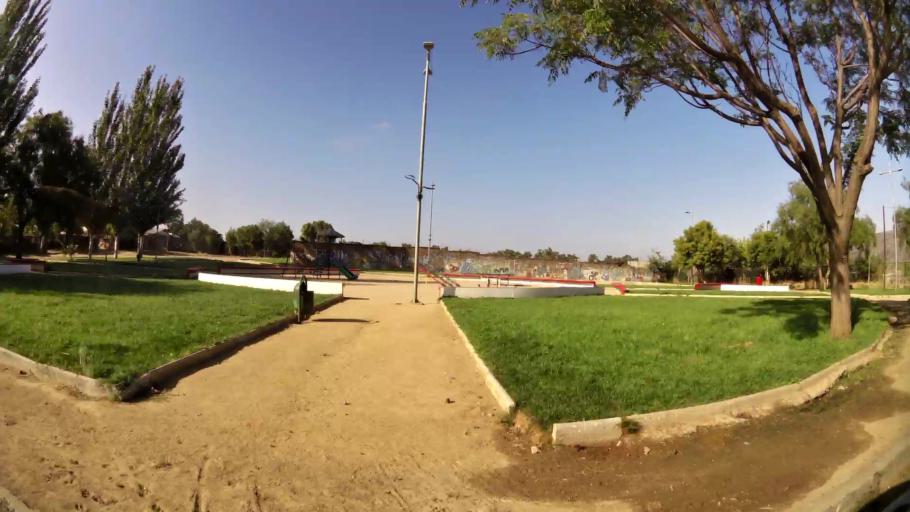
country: CL
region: Maule
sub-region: Provincia de Talca
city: Talca
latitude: -35.4052
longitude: -71.6619
